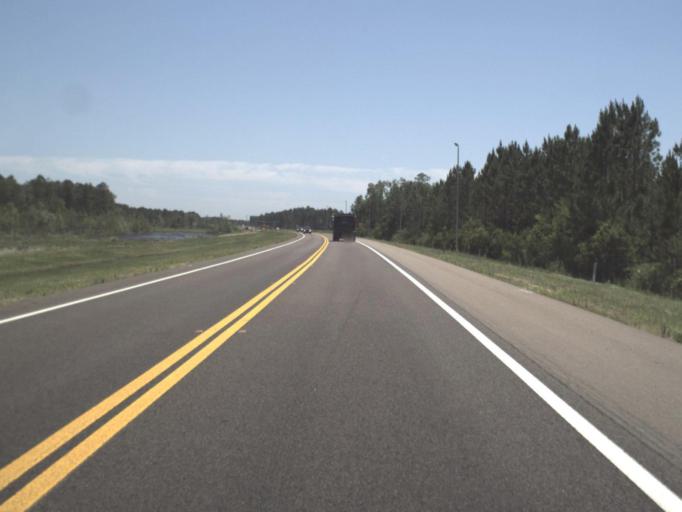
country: US
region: Florida
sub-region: Duval County
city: Baldwin
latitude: 30.2662
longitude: -81.8693
